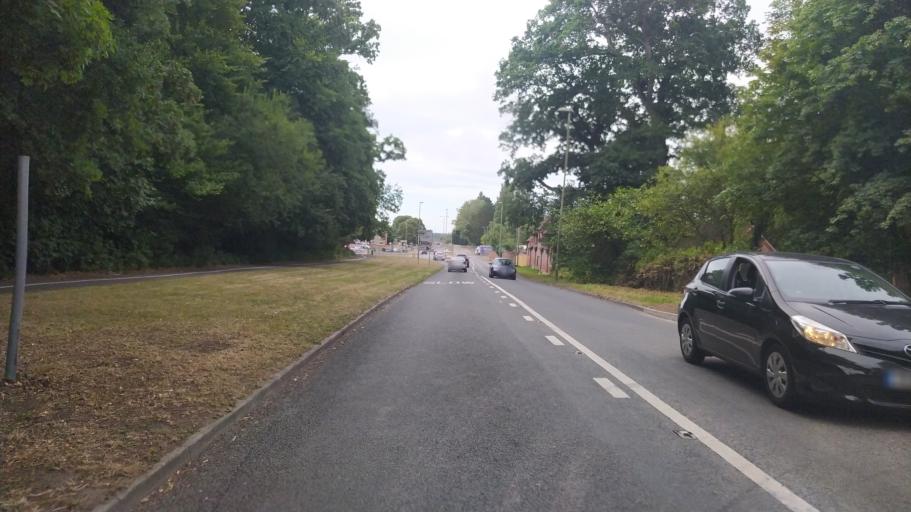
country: GB
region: England
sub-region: Hampshire
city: Havant
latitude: 50.8762
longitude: -0.9735
